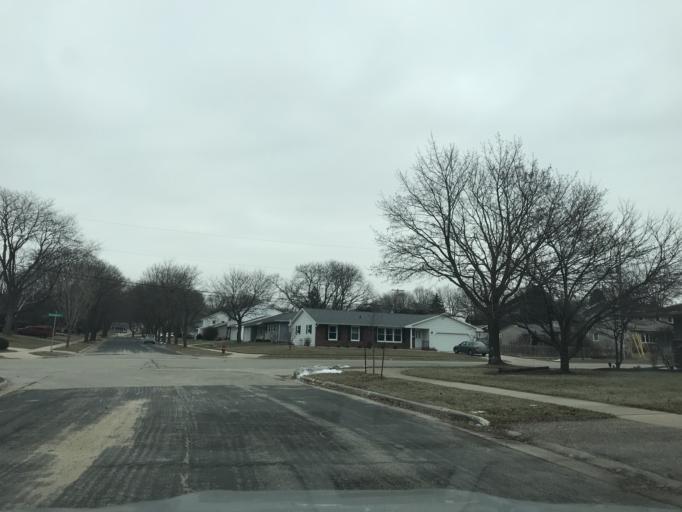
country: US
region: Wisconsin
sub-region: Dane County
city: Monona
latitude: 43.0869
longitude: -89.2974
